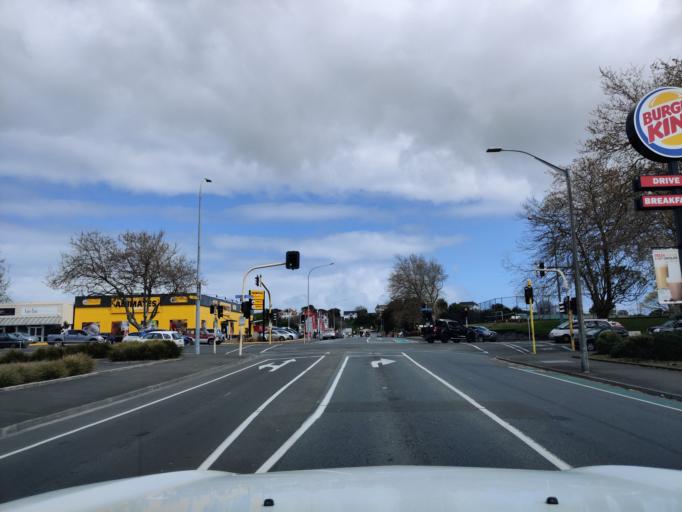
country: NZ
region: Manawatu-Wanganui
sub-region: Wanganui District
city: Wanganui
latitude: -39.9276
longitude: 175.0439
